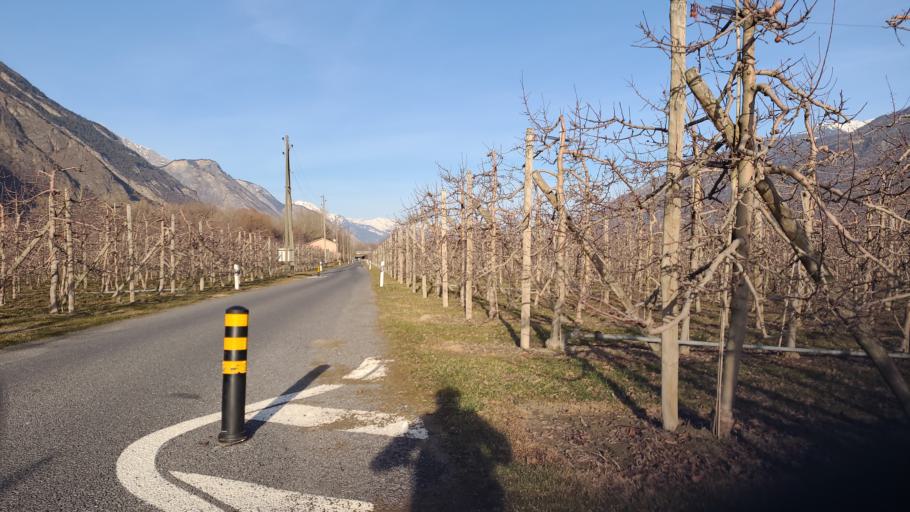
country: CH
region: Valais
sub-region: Martigny District
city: Charrat-les-Chenes
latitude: 46.1446
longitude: 7.1459
